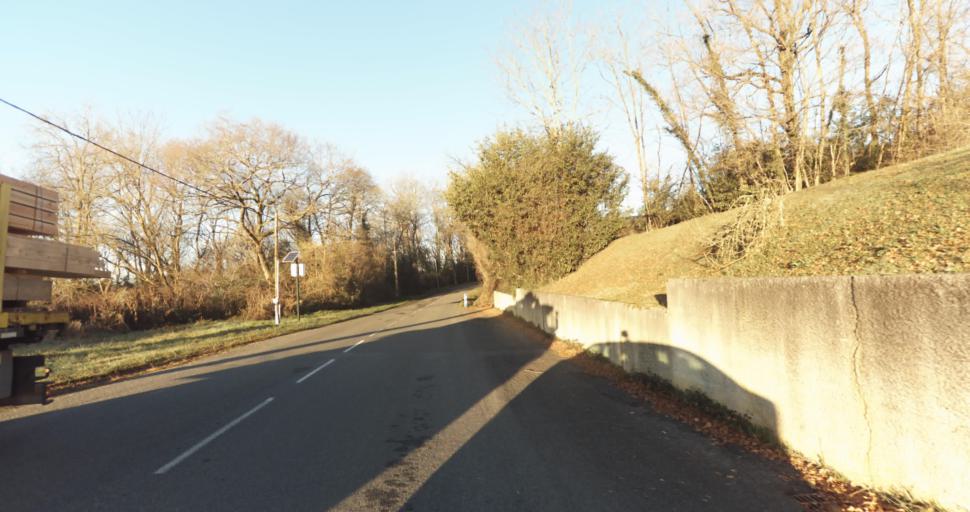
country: FR
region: Aquitaine
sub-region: Departement des Pyrenees-Atlantiques
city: Morlaas
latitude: 43.3278
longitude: -0.2673
